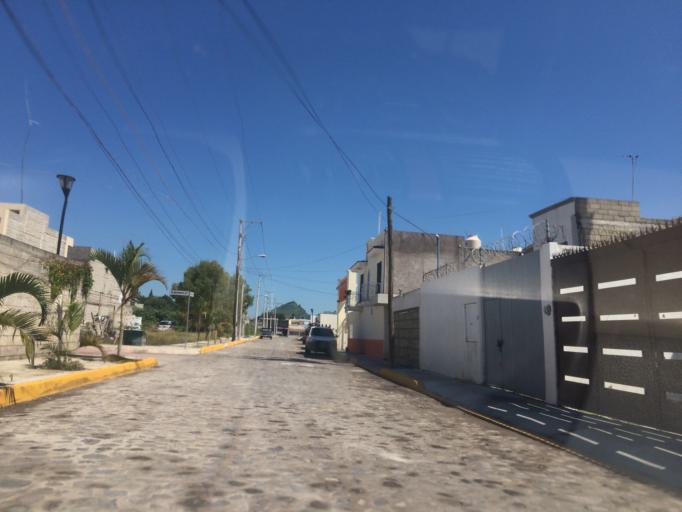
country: MX
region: Nayarit
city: Tepic
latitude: 21.4977
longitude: -104.8787
